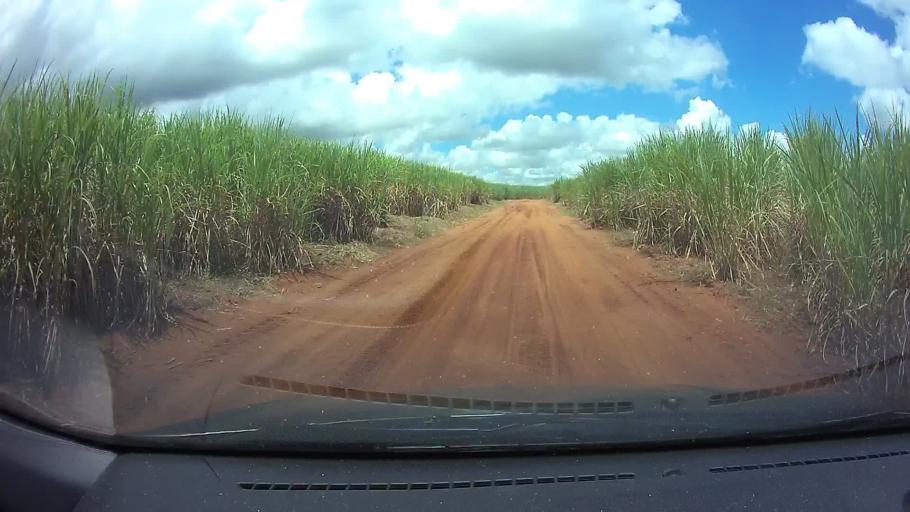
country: PY
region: Paraguari
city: La Colmena
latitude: -25.9623
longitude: -56.7632
